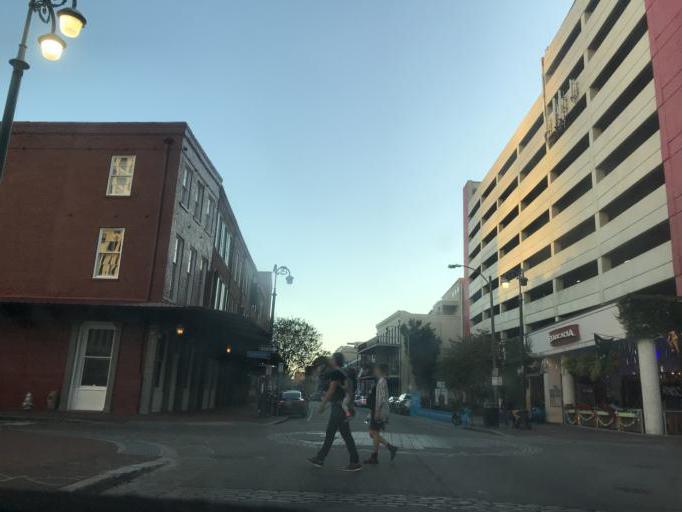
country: US
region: Louisiana
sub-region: Orleans Parish
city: New Orleans
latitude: 29.9478
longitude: -90.0672
